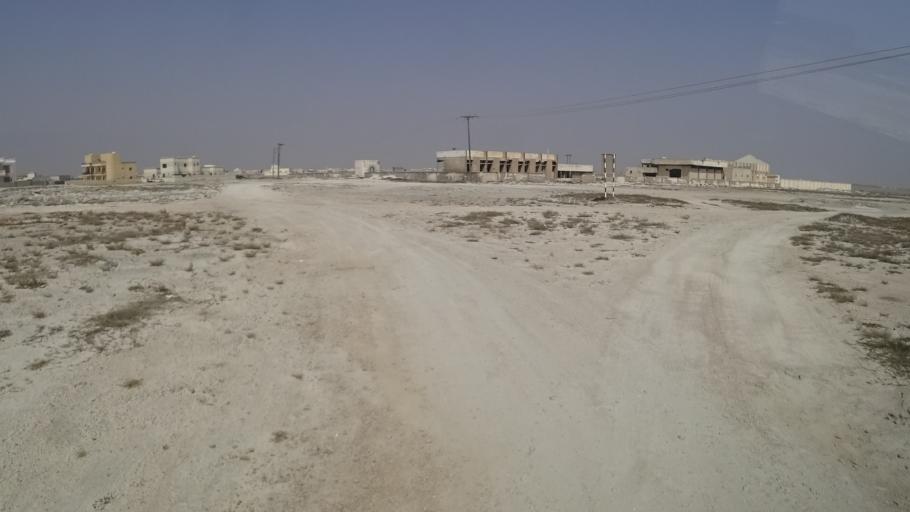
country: OM
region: Zufar
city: Salalah
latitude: 16.9719
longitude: 54.7011
